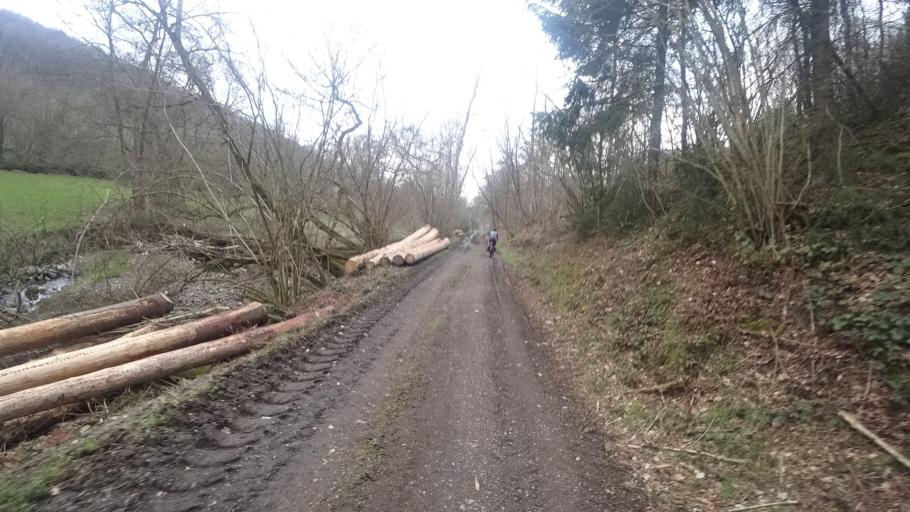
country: DE
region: Rheinland-Pfalz
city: Elben
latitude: 50.7606
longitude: 7.8321
